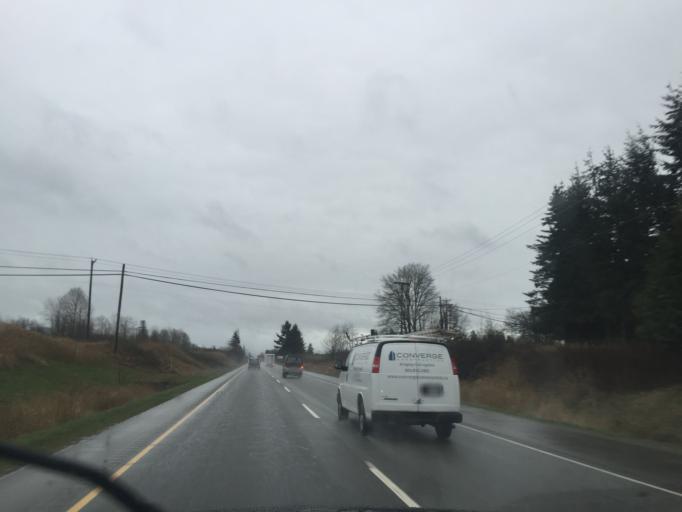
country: CA
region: British Columbia
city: Aldergrove
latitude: 49.0931
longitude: -122.4718
